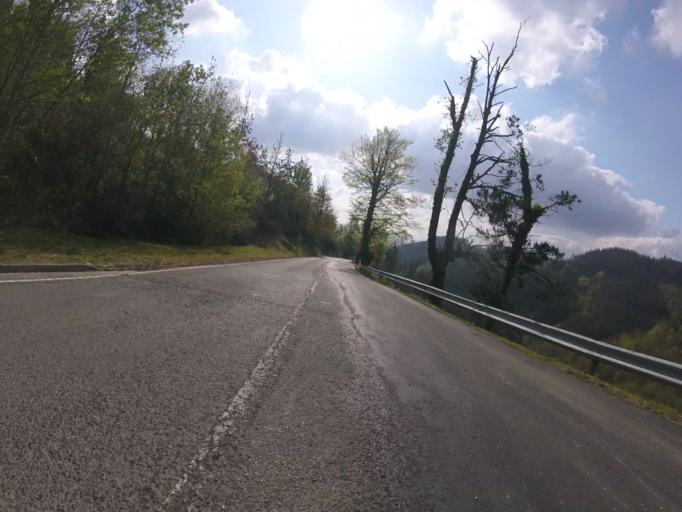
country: ES
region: Basque Country
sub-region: Provincia de Guipuzcoa
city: Azkoitia
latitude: 43.2018
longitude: -2.3542
